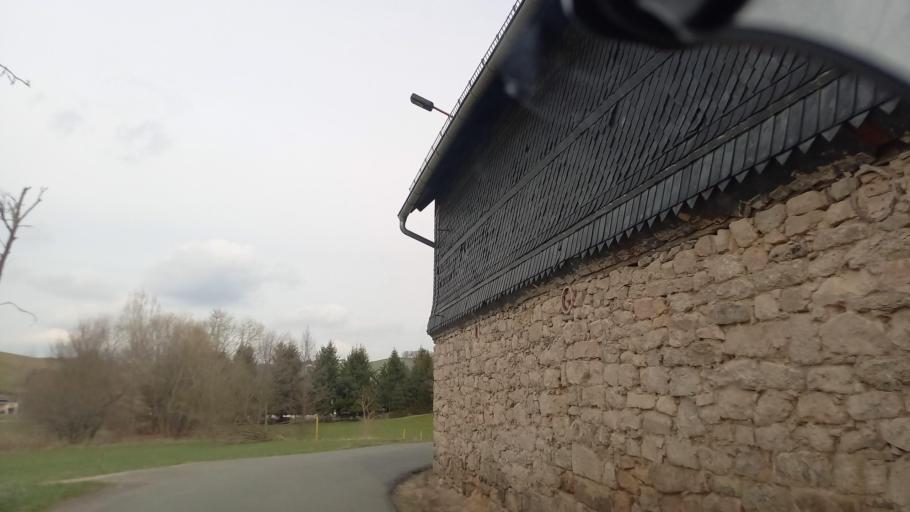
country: DE
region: Saxony
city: Kirchberg
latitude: 50.6400
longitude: 12.5192
